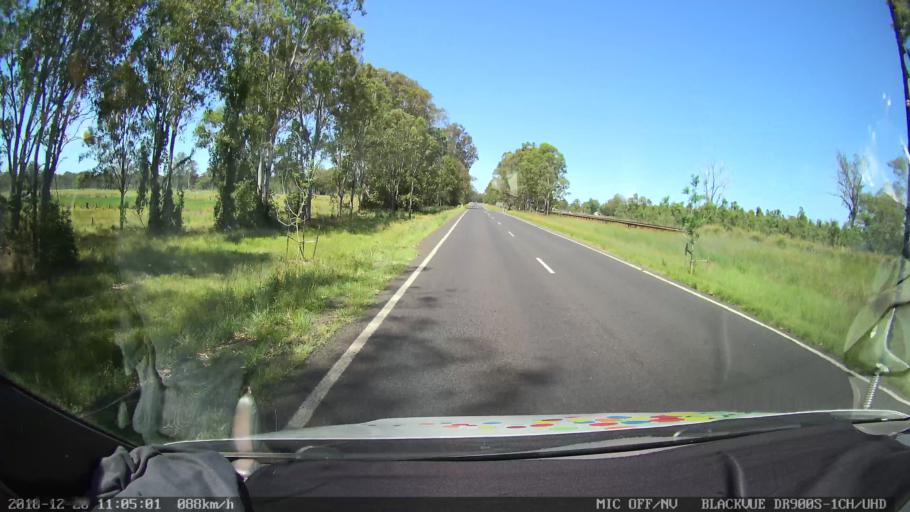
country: AU
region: New South Wales
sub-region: Richmond Valley
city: Casino
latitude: -28.8918
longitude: 153.0446
